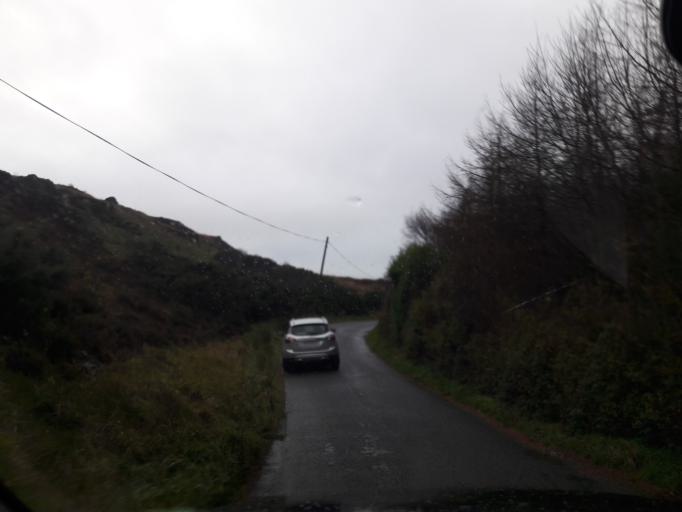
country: IE
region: Ulster
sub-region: County Donegal
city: Buncrana
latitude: 55.2230
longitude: -7.6149
